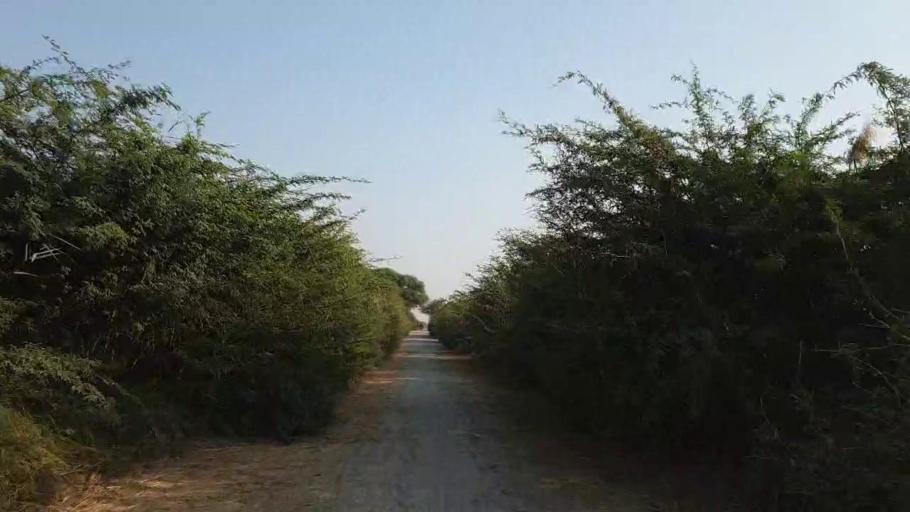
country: PK
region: Sindh
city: Bulri
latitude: 24.9641
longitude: 68.4582
